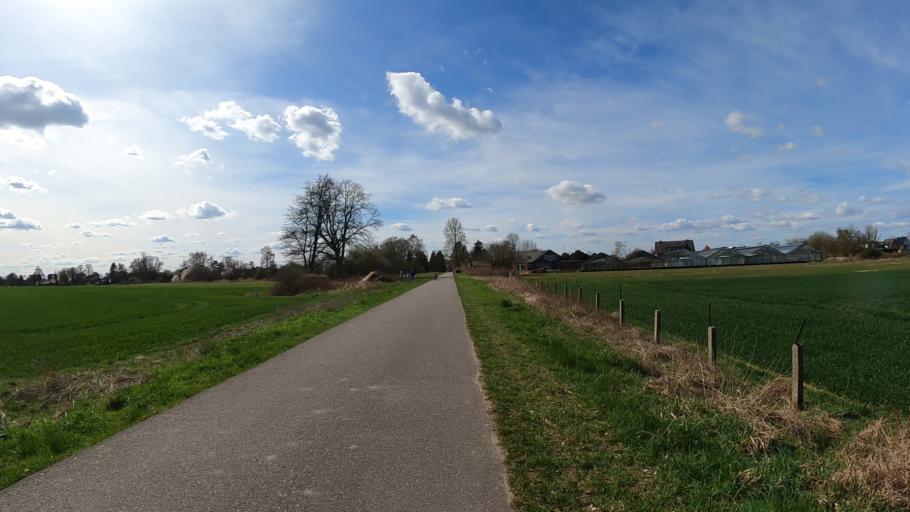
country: DE
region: Lower Saxony
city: Drage
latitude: 53.4323
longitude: 10.2790
